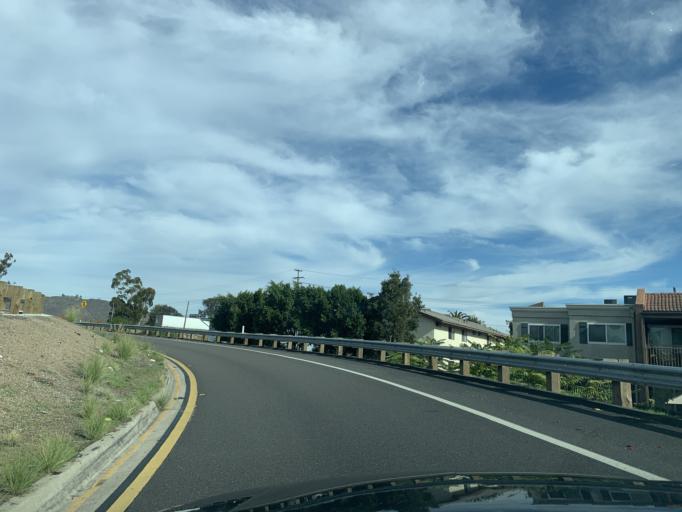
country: US
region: California
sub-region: San Diego County
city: El Cajon
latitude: 32.8020
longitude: -116.9615
